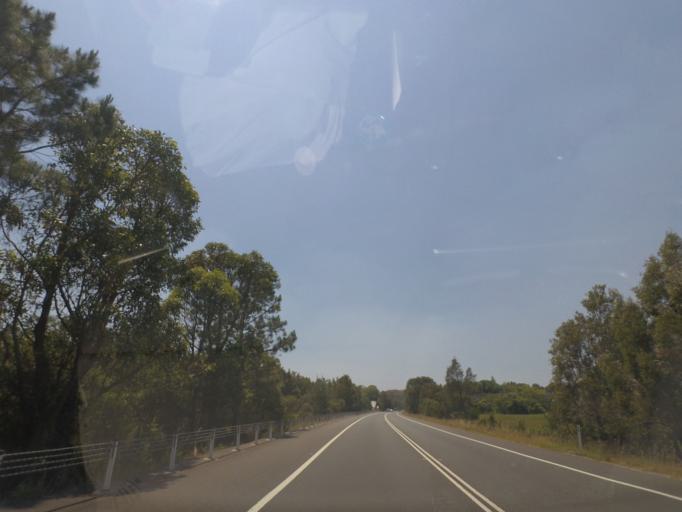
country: AU
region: New South Wales
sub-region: Port Stephens Shire
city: Medowie
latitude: -32.8073
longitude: 151.8589
